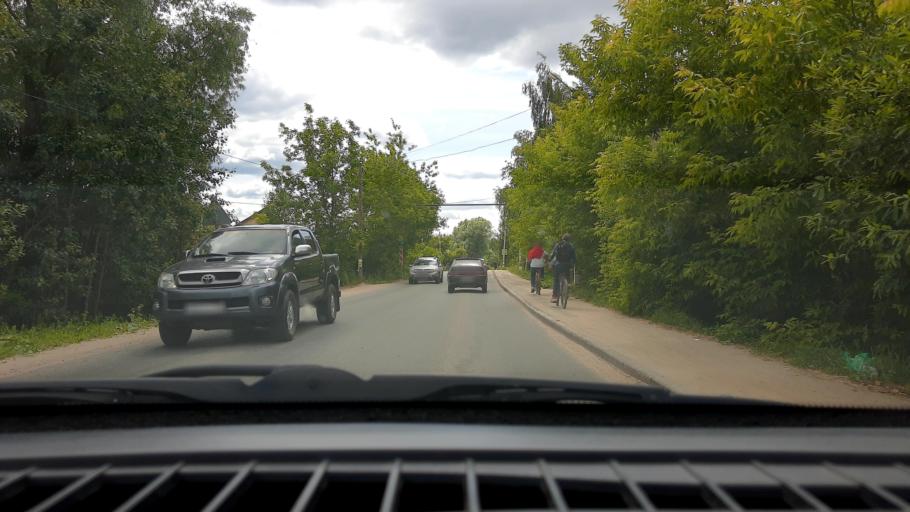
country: RU
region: Nizjnij Novgorod
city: Bor
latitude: 56.3856
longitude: 44.0417
